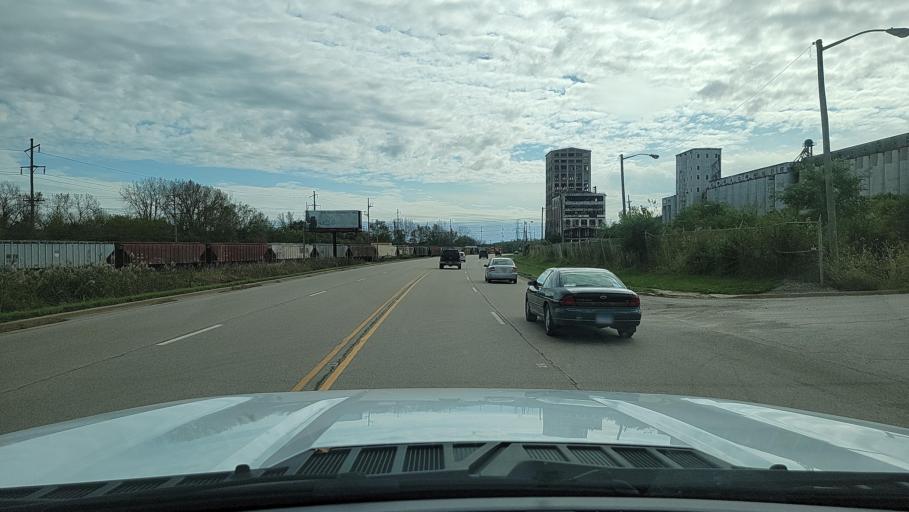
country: US
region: Illinois
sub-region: Peoria County
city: Bartonville
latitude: 40.6355
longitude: -89.6515
